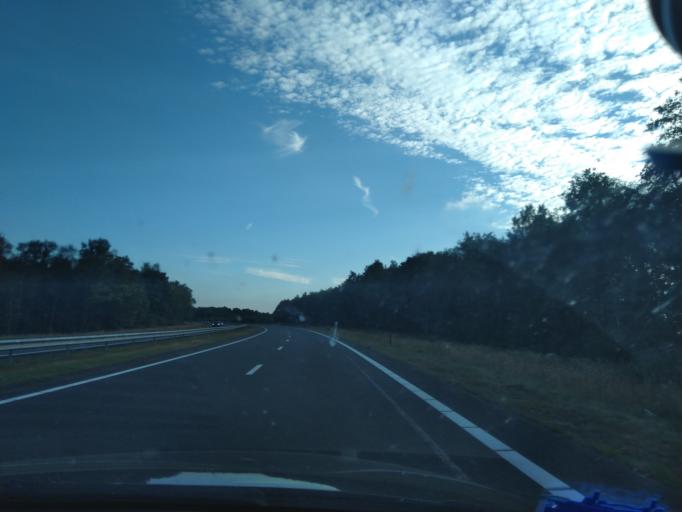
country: NL
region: Drenthe
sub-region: Gemeente Aa en Hunze
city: Anloo
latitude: 52.9989
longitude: 6.6988
